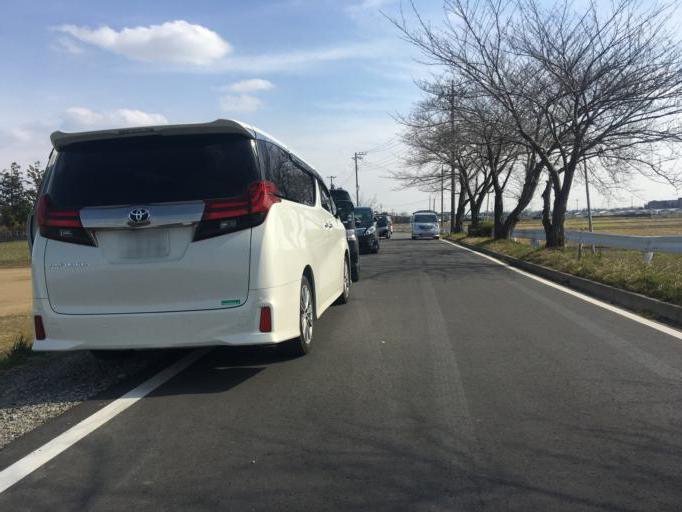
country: JP
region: Saitama
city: Oi
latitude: 35.8729
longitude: 139.5596
